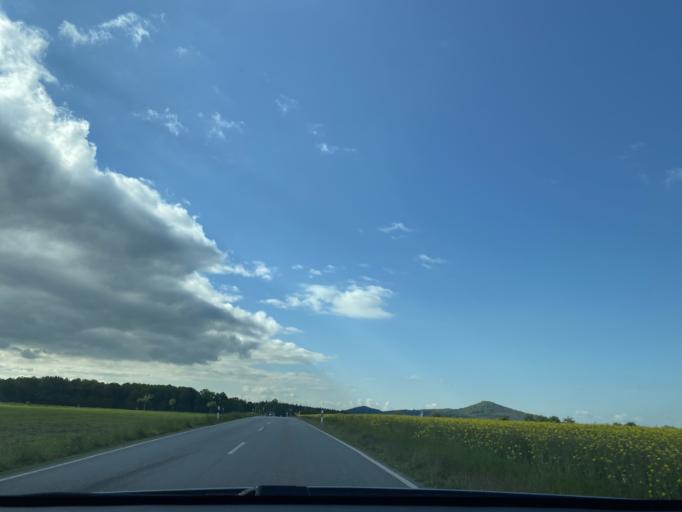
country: DE
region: Saxony
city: Sohland am Rotstein
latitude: 51.0737
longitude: 14.7744
